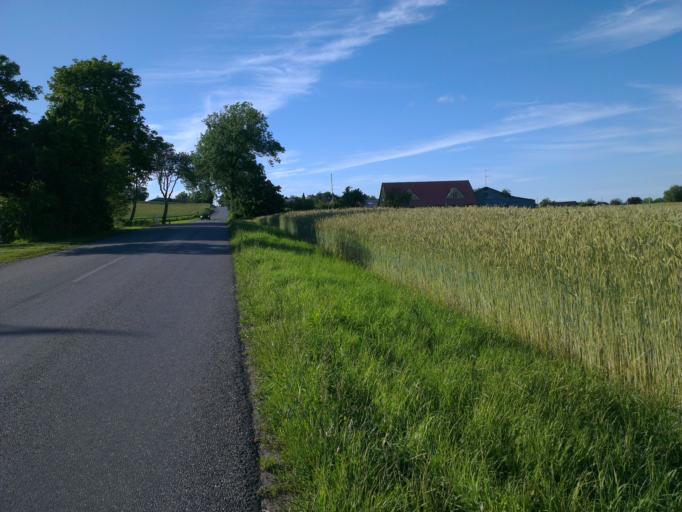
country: DK
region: Capital Region
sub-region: Frederikssund Kommune
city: Skibby
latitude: 55.7717
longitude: 12.0236
